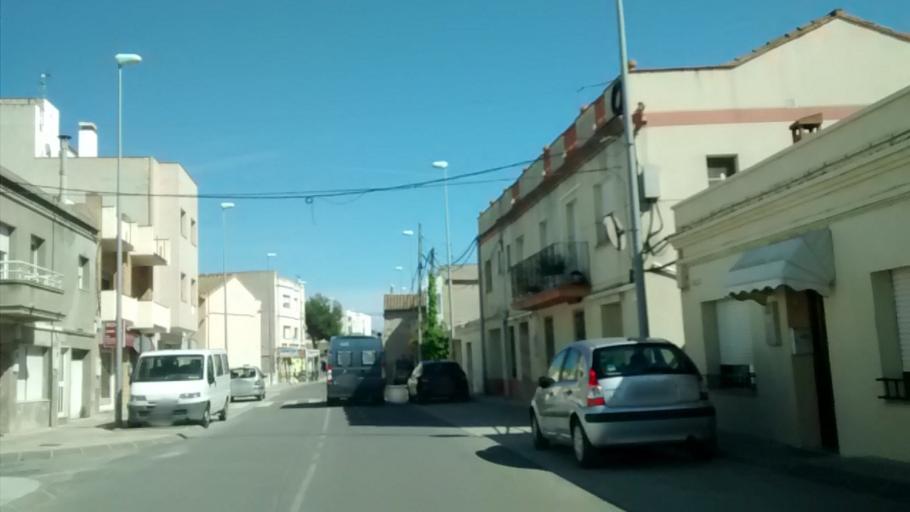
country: ES
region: Catalonia
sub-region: Provincia de Tarragona
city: Deltebre
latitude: 40.7162
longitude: 0.7432
